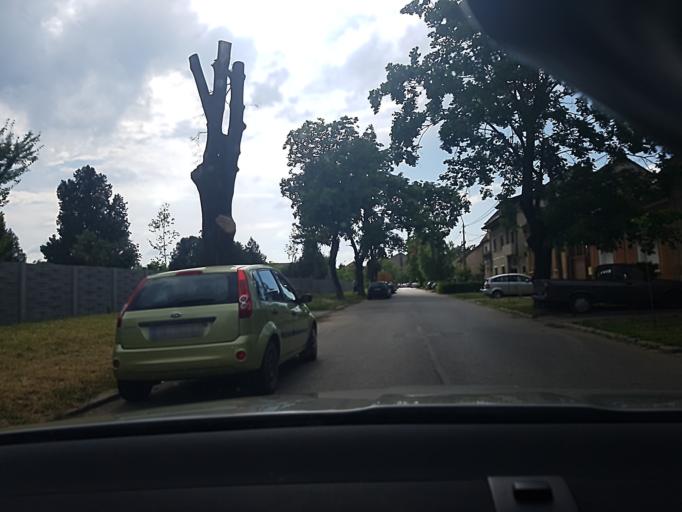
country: RO
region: Timis
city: Timisoara
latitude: 45.7379
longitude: 21.2203
